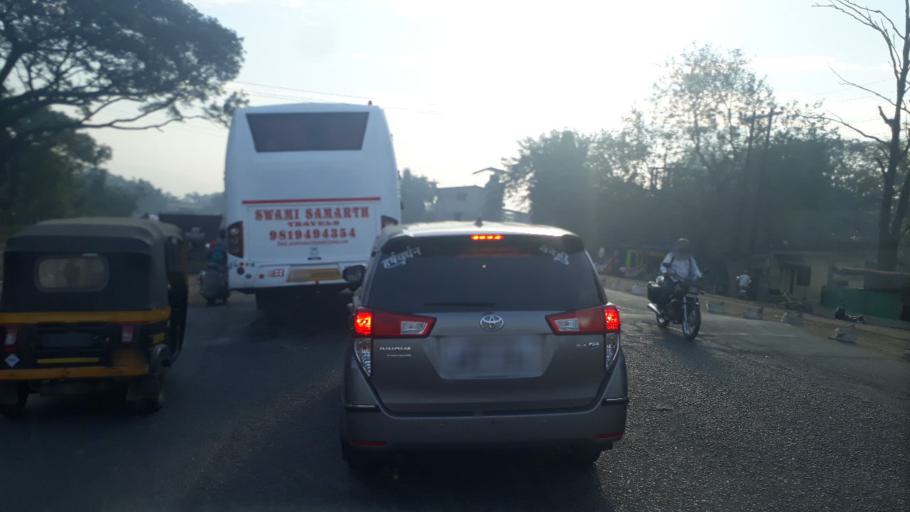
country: IN
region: Maharashtra
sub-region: Raigarh
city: Kalundri
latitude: 18.9750
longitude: 73.1186
